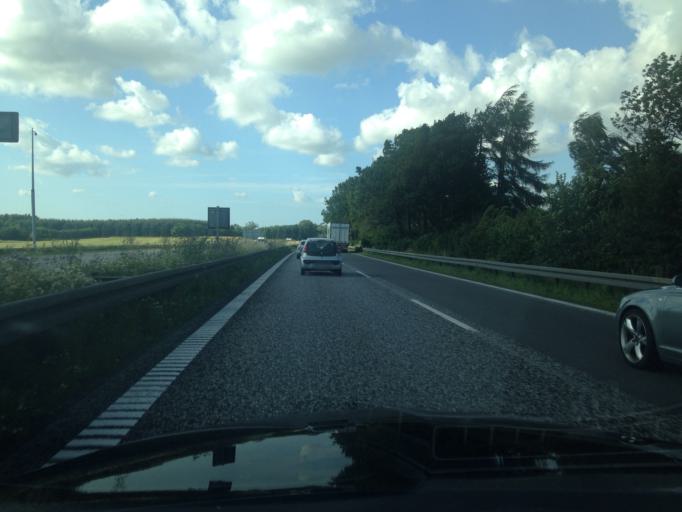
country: DK
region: Capital Region
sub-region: Horsholm Kommune
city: Horsholm
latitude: 55.8802
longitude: 12.4801
